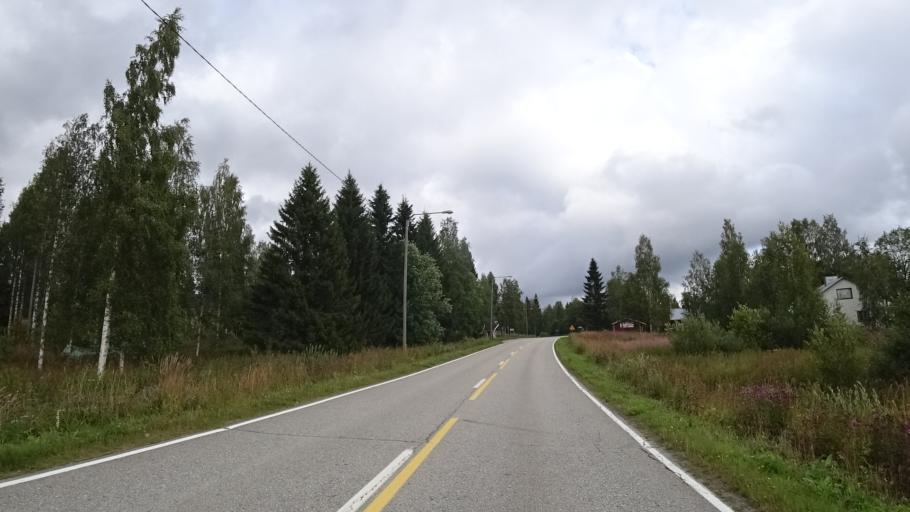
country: FI
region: North Karelia
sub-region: Joensuu
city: Ilomantsi
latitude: 62.9309
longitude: 31.2794
